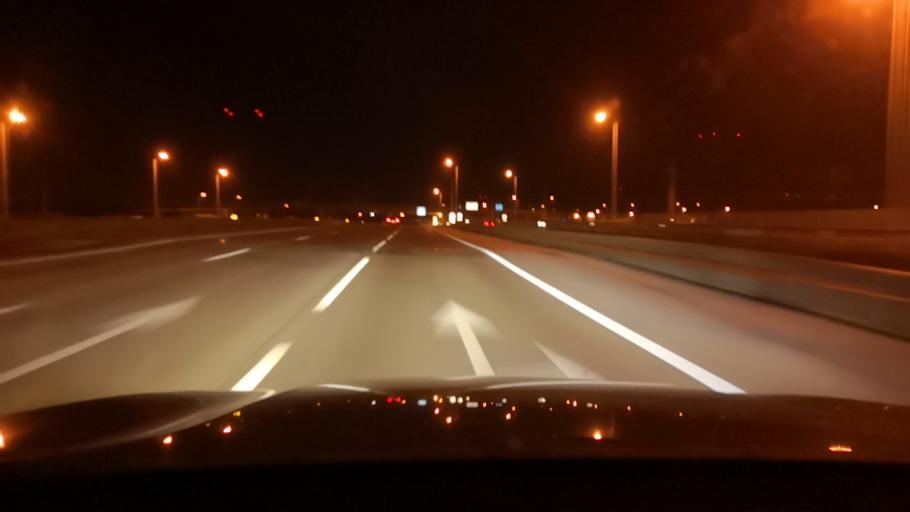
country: PT
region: Lisbon
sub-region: Alenquer
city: Carregado
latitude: 39.0124
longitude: -8.9662
